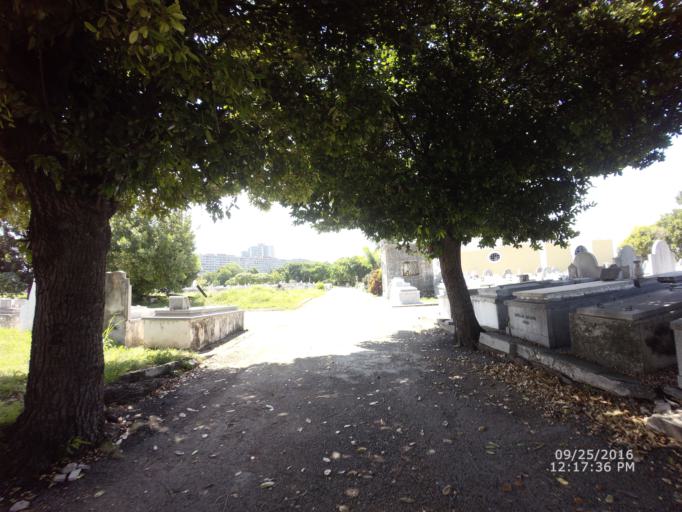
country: CU
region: La Habana
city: Havana
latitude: 23.1217
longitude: -82.3970
